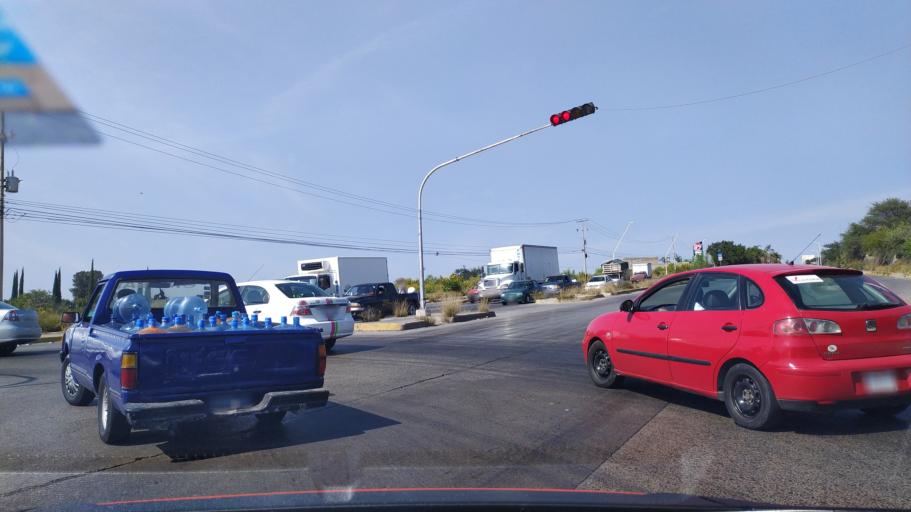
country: MX
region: Jalisco
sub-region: Tlajomulco de Zuniga
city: Altus Bosques
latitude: 20.5922
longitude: -103.3809
